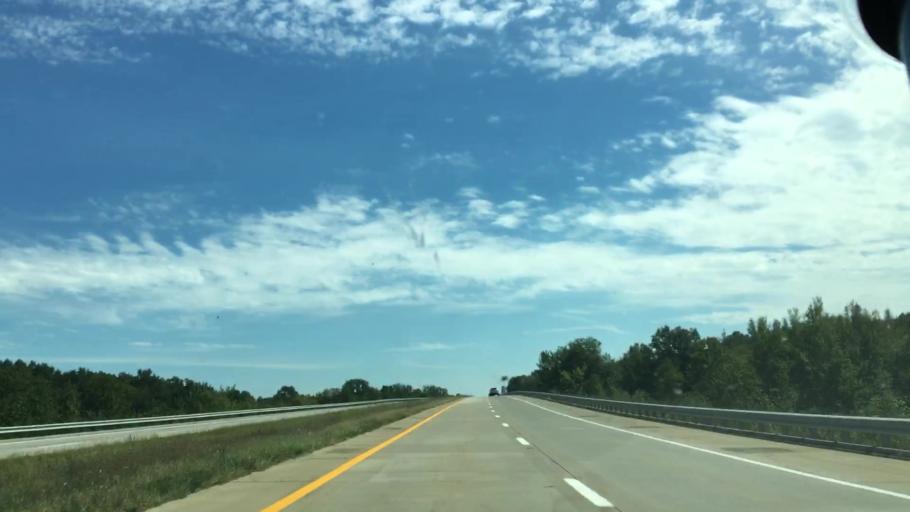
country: US
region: Kentucky
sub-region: Daviess County
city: Owensboro
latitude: 37.7595
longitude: -87.3006
